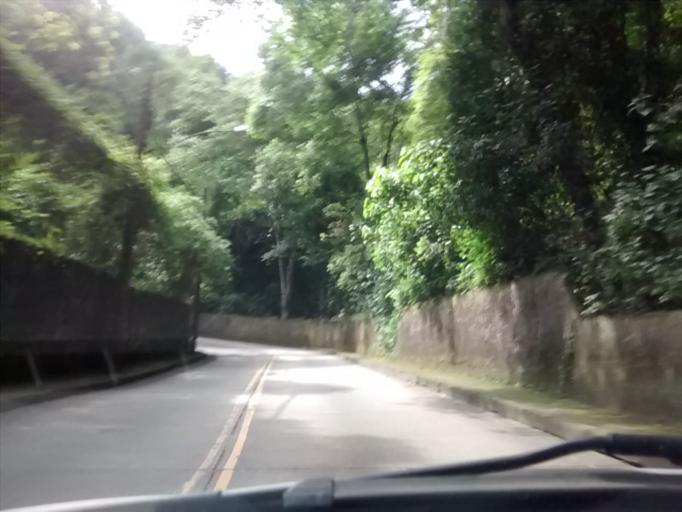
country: BR
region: Rio de Janeiro
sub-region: Rio De Janeiro
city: Rio de Janeiro
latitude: -22.9744
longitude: -43.2801
